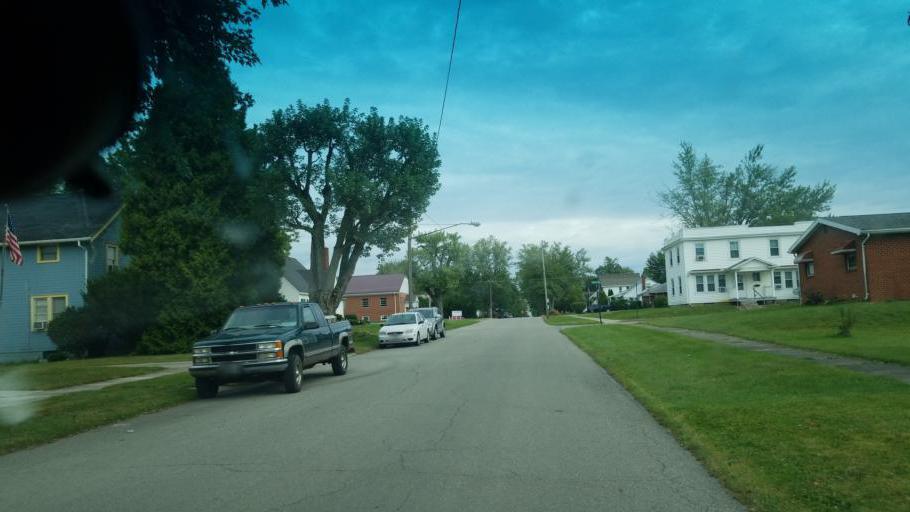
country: US
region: Ohio
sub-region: Crawford County
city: Crestline
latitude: 40.7878
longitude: -82.7476
